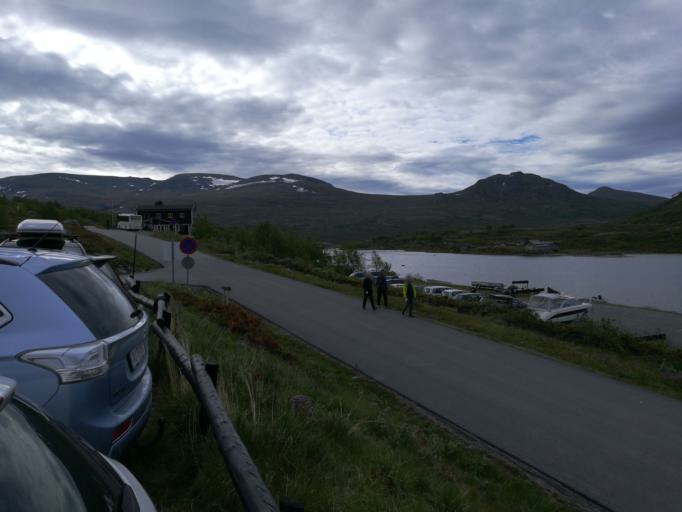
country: NO
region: Oppland
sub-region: Lom
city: Fossbergom
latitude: 61.4953
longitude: 8.8101
